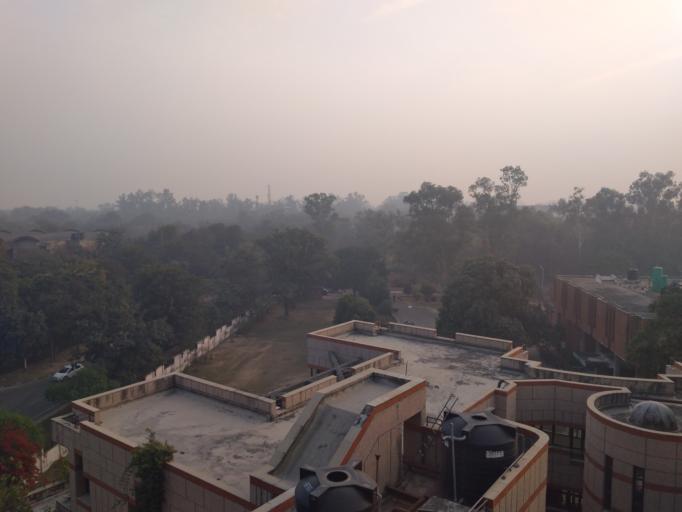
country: IN
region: Uttar Pradesh
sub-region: Kanpur
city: Nawabganj
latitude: 26.5143
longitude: 80.2349
